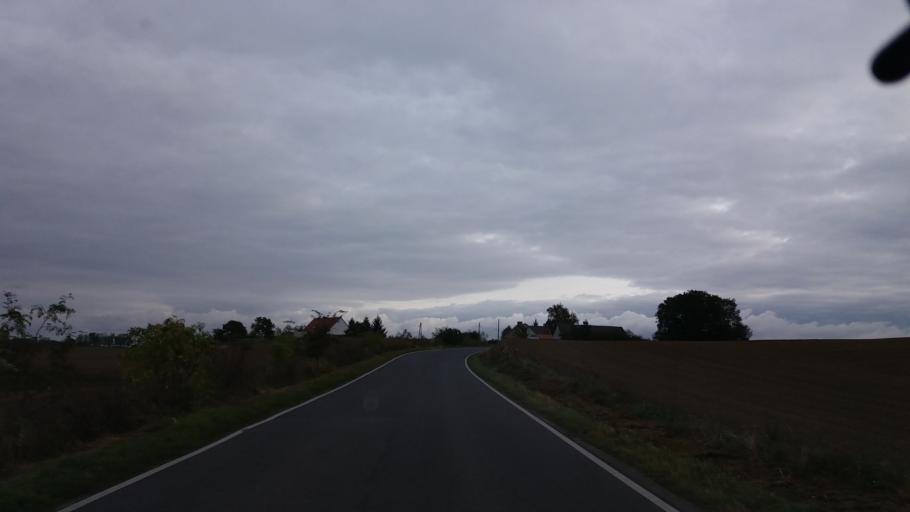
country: PL
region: West Pomeranian Voivodeship
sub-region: Powiat choszczenski
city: Pelczyce
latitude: 53.0319
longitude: 15.3491
